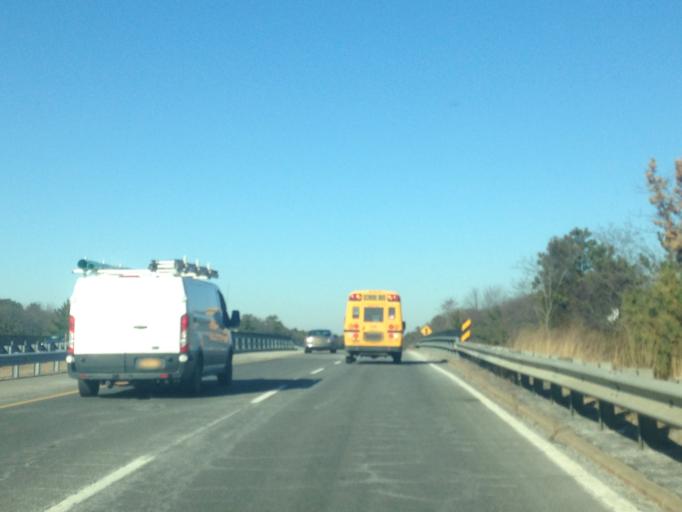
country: US
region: New York
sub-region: Suffolk County
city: Holtsville
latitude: 40.7898
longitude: -73.0514
